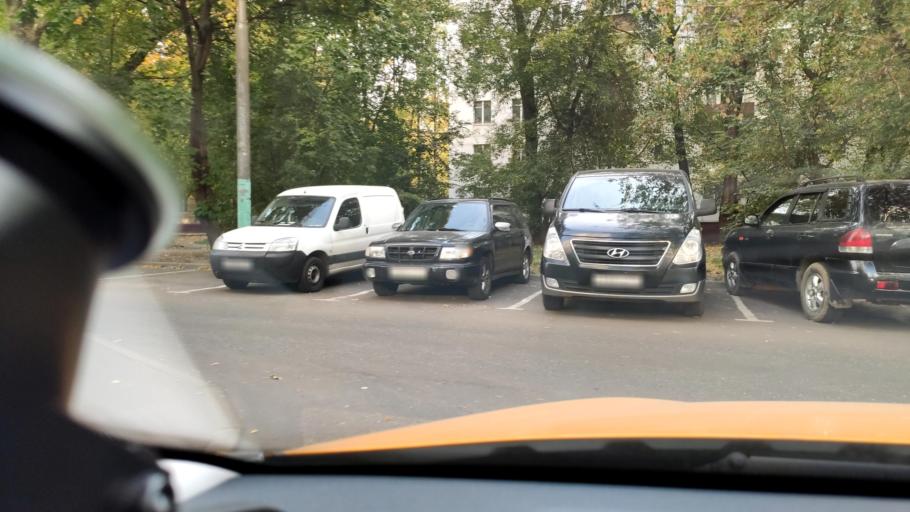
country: RU
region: Moscow
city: Perovo
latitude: 55.7404
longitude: 37.7793
